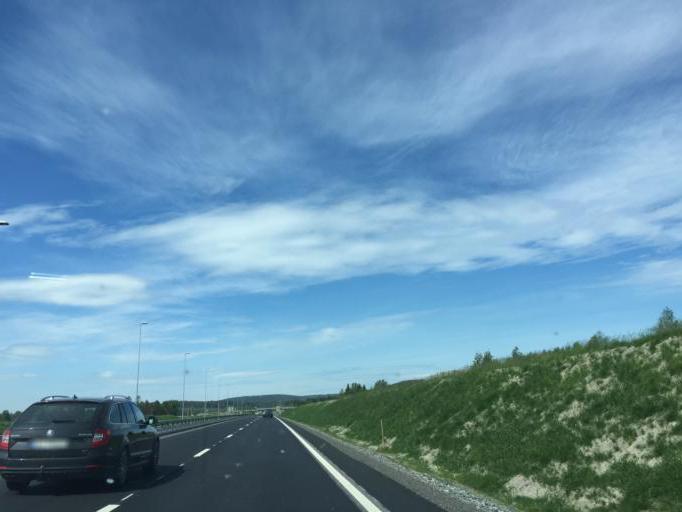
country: NO
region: Hedmark
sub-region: Sor-Odal
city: Skarnes
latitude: 60.2462
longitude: 11.7575
